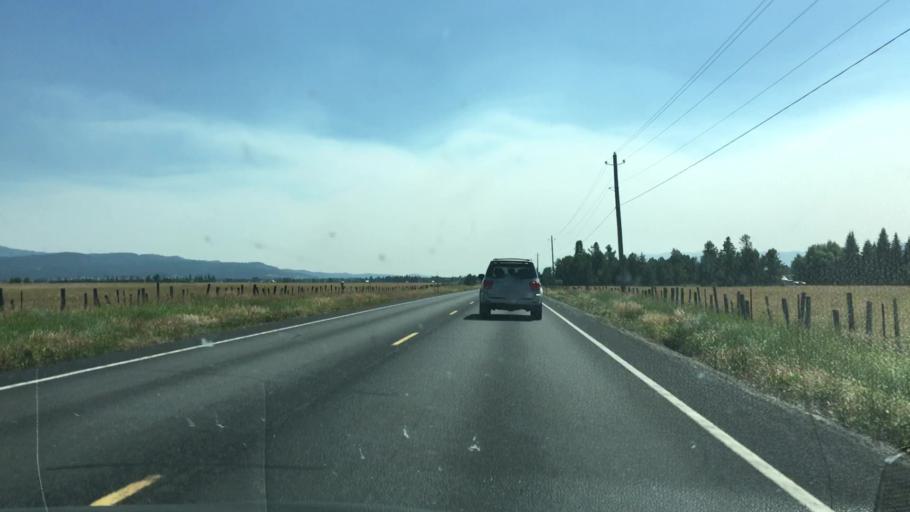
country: US
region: Idaho
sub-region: Valley County
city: McCall
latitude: 44.7596
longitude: -116.0782
